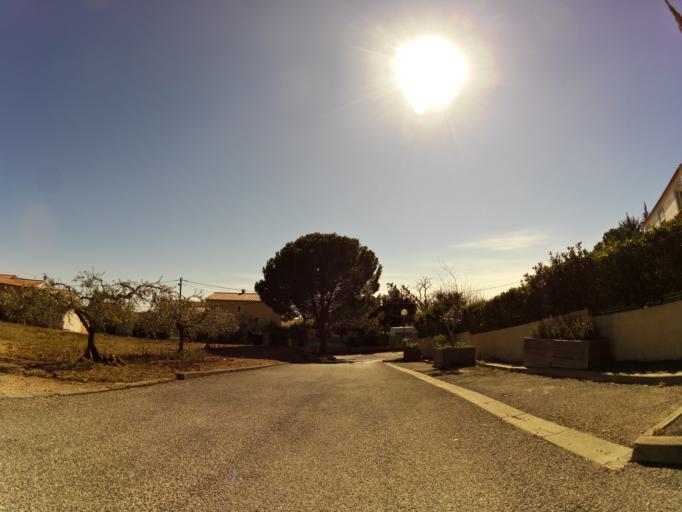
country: FR
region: Languedoc-Roussillon
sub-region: Departement du Gard
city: Mus
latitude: 43.7359
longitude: 4.2066
